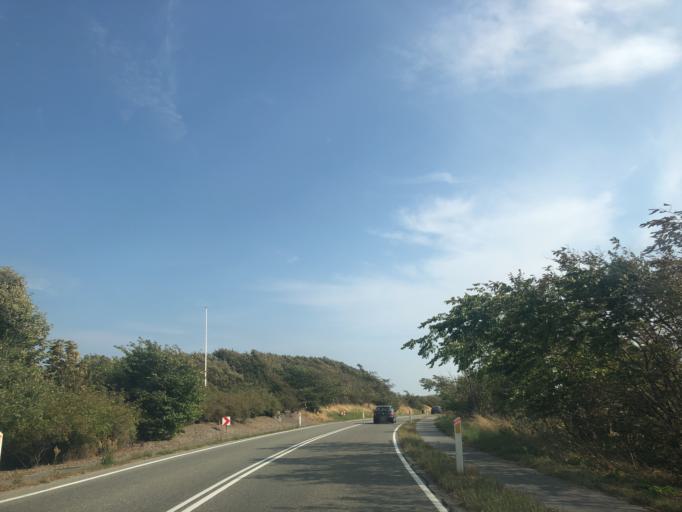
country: DK
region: North Denmark
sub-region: Morso Kommune
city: Nykobing Mors
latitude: 56.7929
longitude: 9.0425
